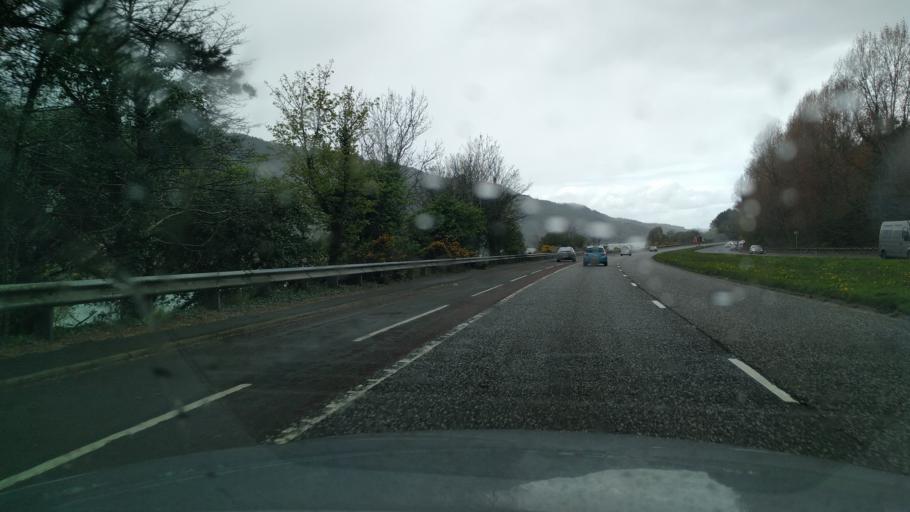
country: GB
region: Northern Ireland
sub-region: Down District
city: Warrenpoint
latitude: 54.1153
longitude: -6.2918
